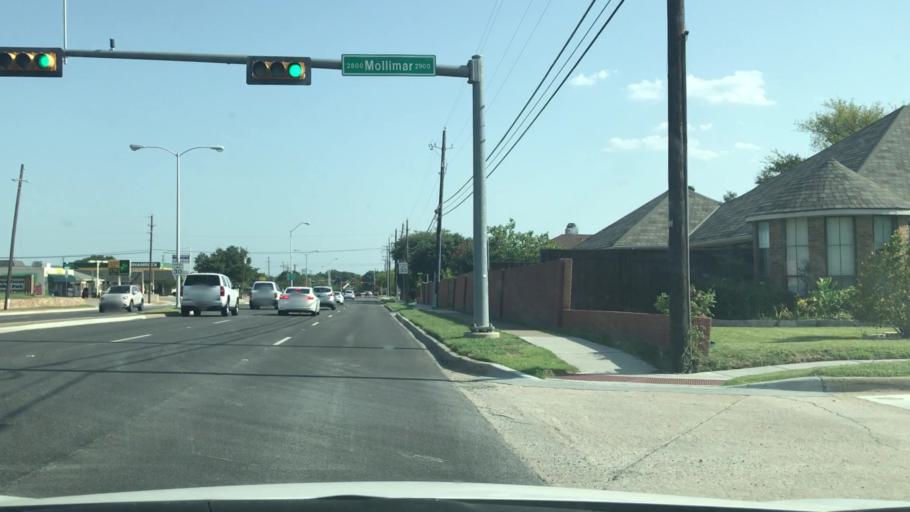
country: US
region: Texas
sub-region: Collin County
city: Plano
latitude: 33.0225
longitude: -96.7500
